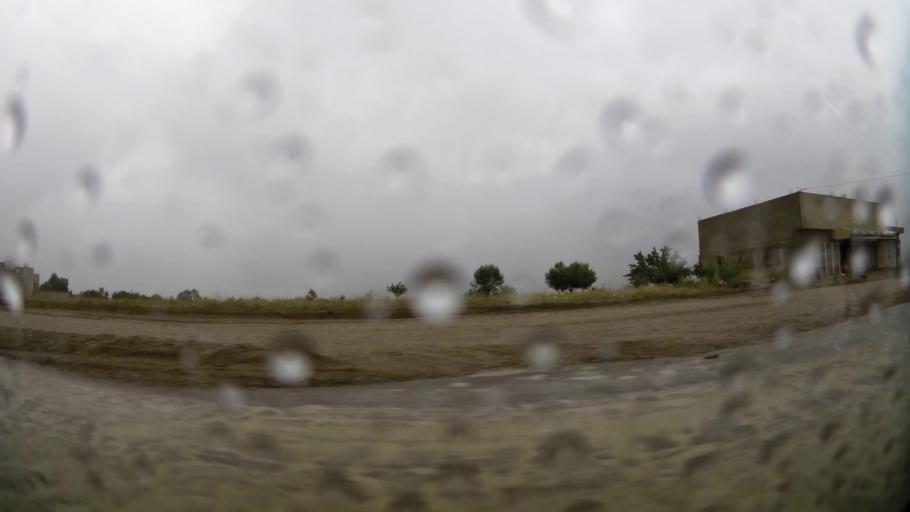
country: MA
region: Oriental
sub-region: Nador
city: Midar
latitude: 34.8745
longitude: -3.7259
